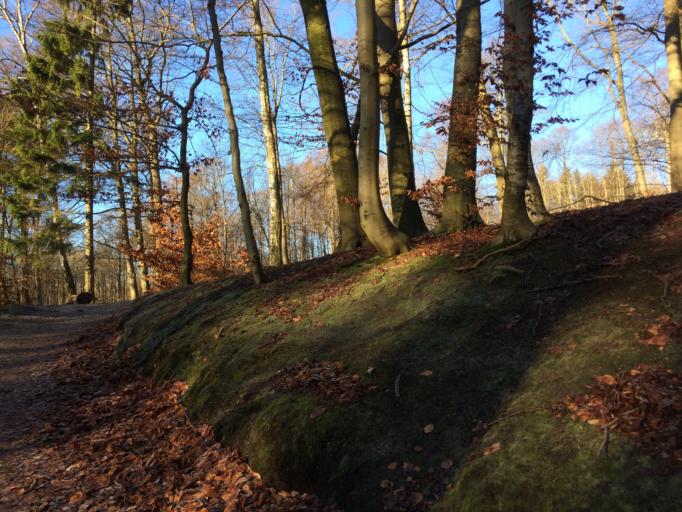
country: DK
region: Capital Region
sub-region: Rudersdal Kommune
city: Holte
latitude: 55.7793
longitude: 12.4565
